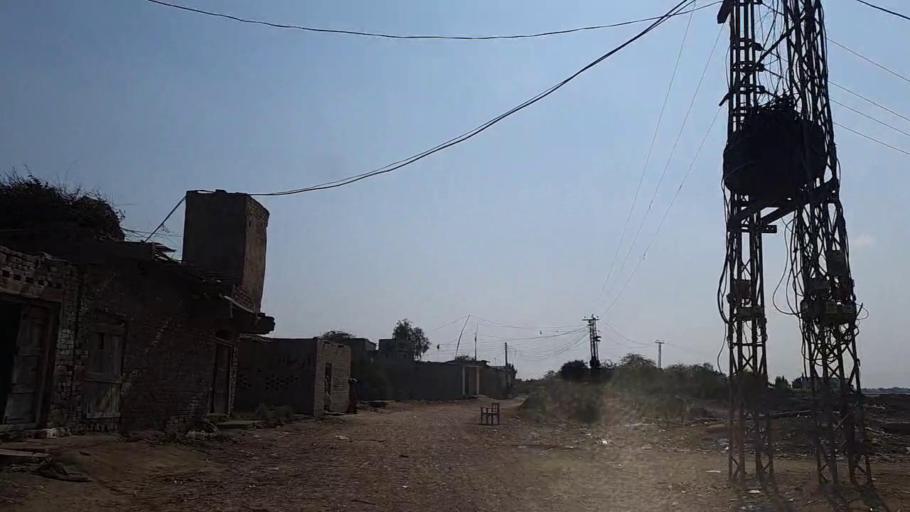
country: PK
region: Sindh
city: Daur
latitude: 26.4611
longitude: 68.2517
